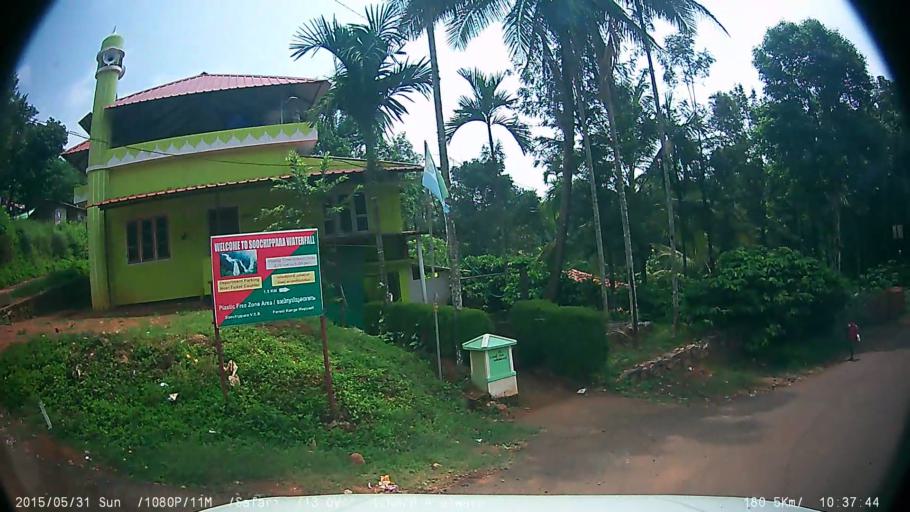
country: IN
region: Kerala
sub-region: Wayanad
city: Kalpetta
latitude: 11.5090
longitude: 76.1511
